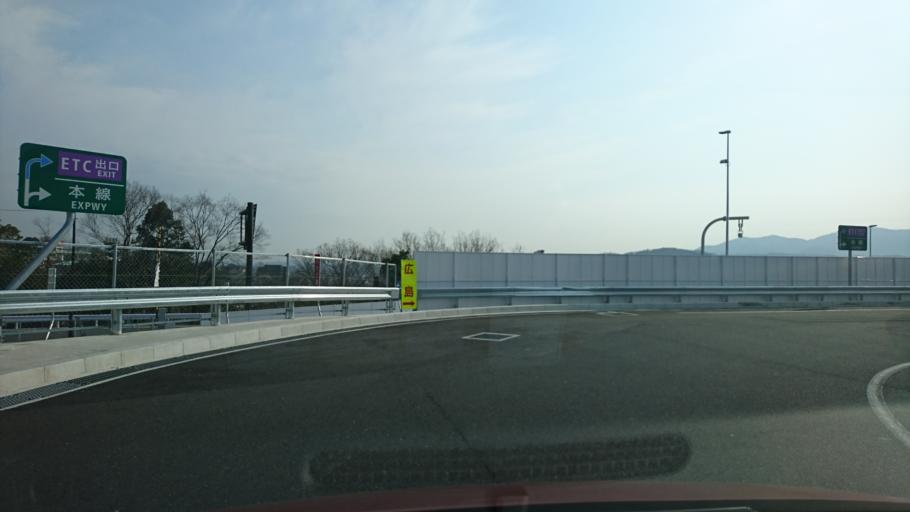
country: JP
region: Hiroshima
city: Fukuyama
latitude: 34.4910
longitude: 133.3165
